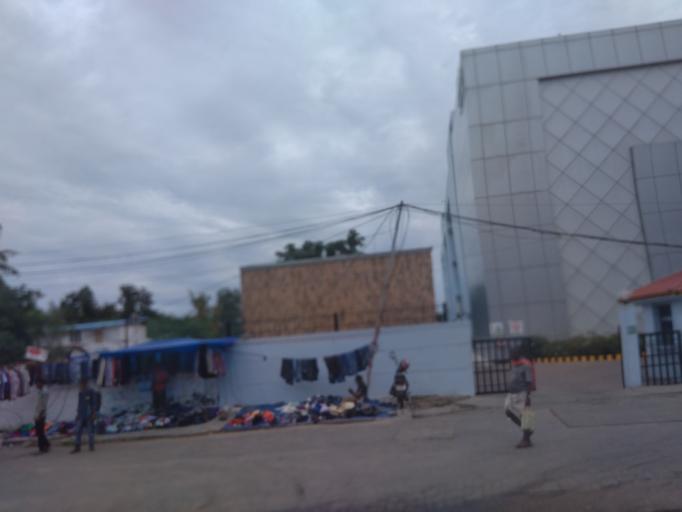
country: IN
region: Tamil Nadu
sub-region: Kancheepuram
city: Injambakkam
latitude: 12.8427
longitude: 80.2269
